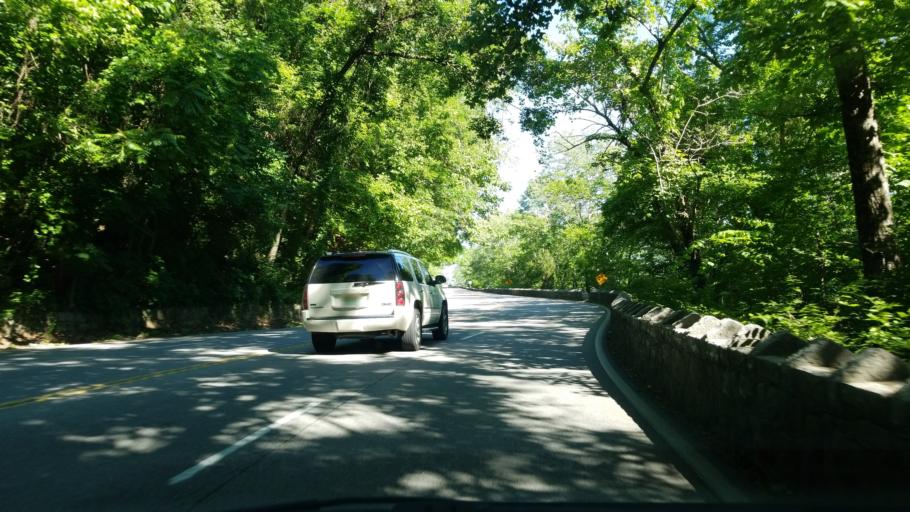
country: US
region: Tennessee
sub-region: Hamilton County
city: Lookout Mountain
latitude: 35.0178
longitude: -85.3348
